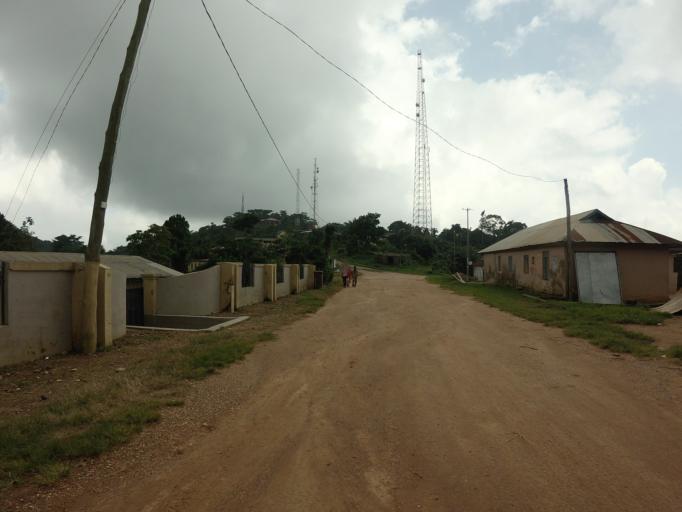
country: TG
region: Plateaux
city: Kpalime
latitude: 6.8437
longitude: 0.4351
